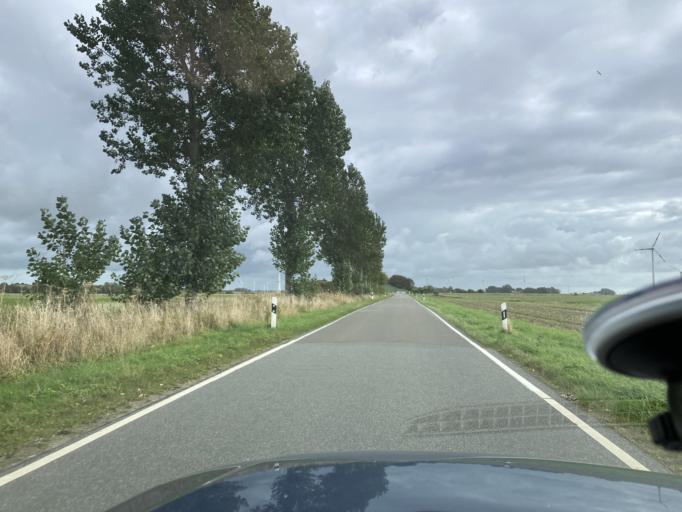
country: DE
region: Schleswig-Holstein
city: Reinsbuttel
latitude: 54.1759
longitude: 8.9208
